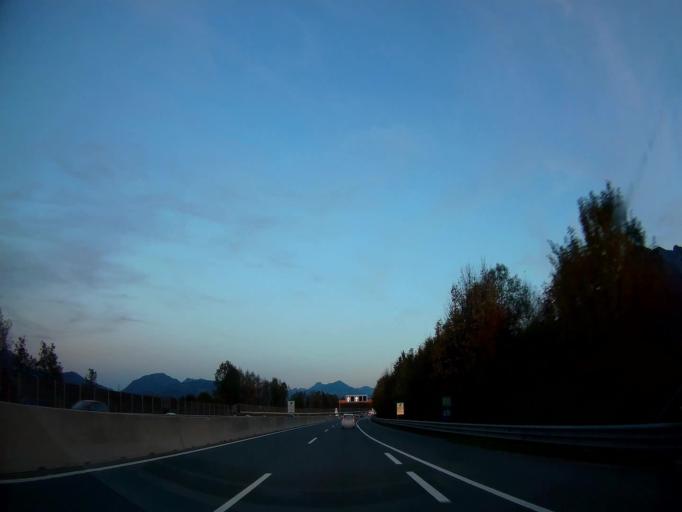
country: AT
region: Salzburg
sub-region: Politischer Bezirk Salzburg-Umgebung
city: Grodig
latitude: 47.7666
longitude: 12.9926
